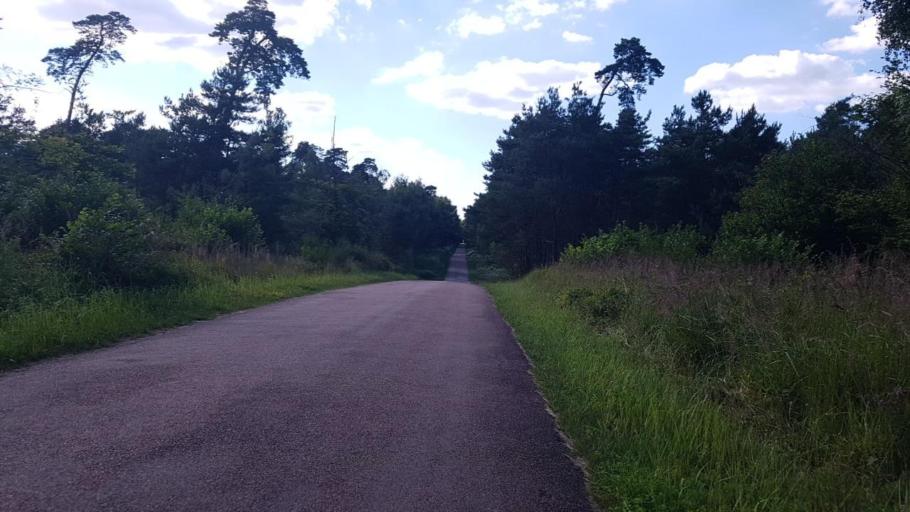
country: FR
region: Picardie
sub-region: Departement de l'Oise
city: Ver-sur-Launette
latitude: 49.1471
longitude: 2.6459
